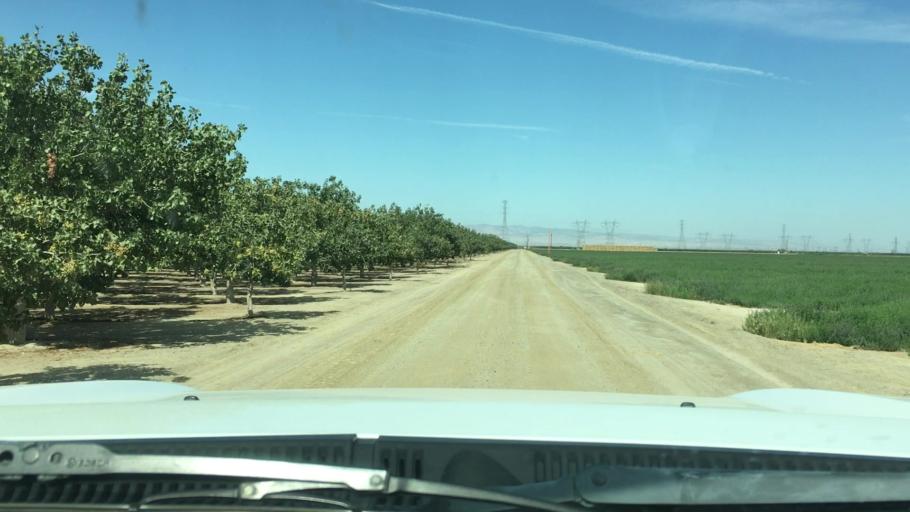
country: US
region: California
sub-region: Kern County
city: Buttonwillow
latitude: 35.3767
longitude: -119.3880
